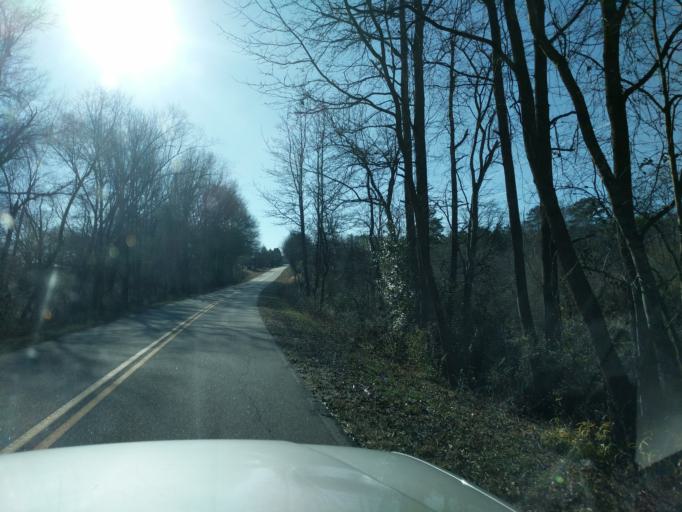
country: US
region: Georgia
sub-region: Hart County
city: Hartwell
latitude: 34.3358
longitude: -82.8648
